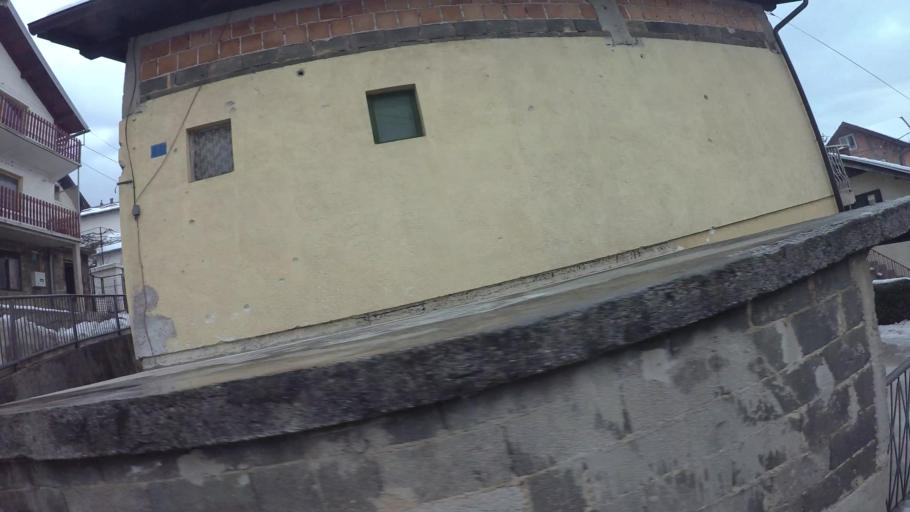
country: BA
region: Federation of Bosnia and Herzegovina
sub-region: Kanton Sarajevo
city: Sarajevo
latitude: 43.8561
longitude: 18.3305
